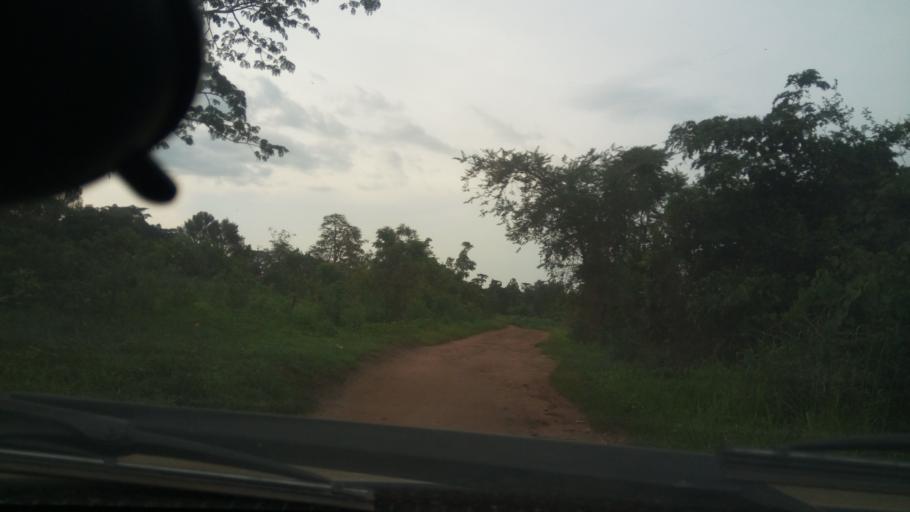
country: UG
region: Central Region
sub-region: Mityana District
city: Mityana
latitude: 0.5657
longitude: 32.1962
